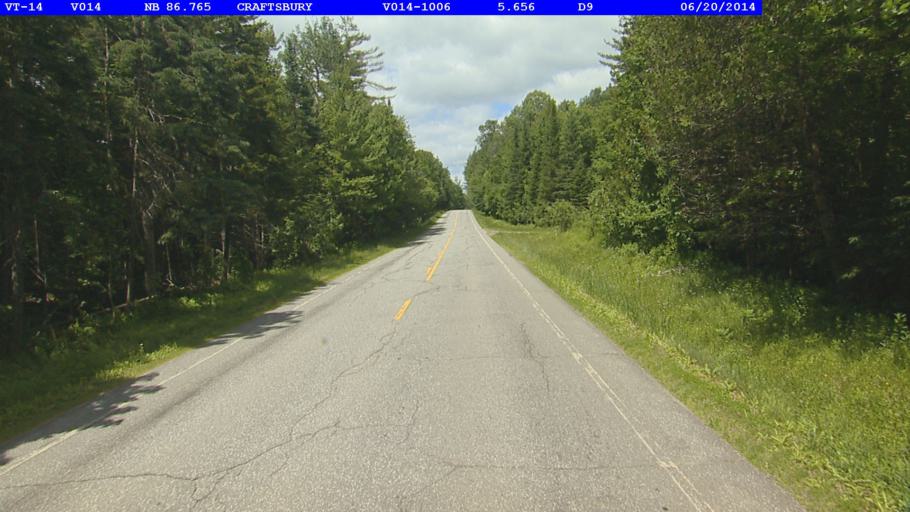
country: US
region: Vermont
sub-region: Caledonia County
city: Hardwick
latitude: 44.6720
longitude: -72.4048
